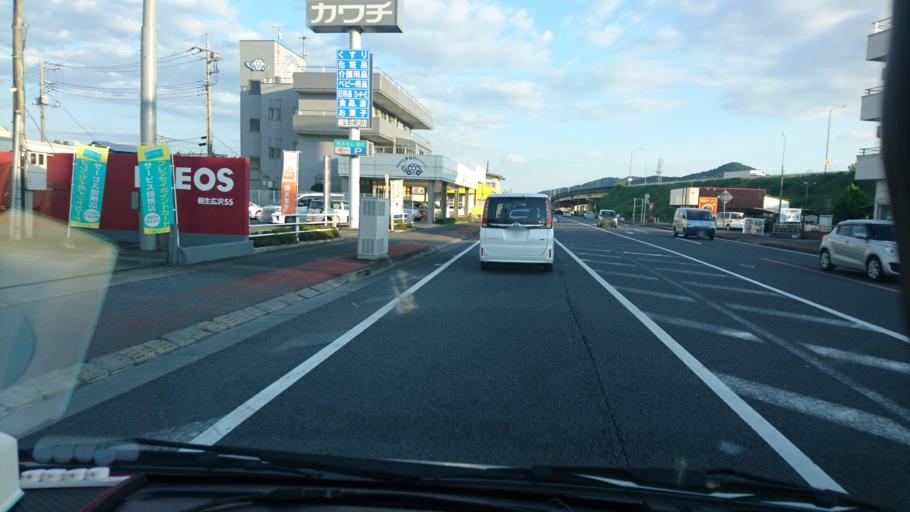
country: JP
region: Gunma
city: Kiryu
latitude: 36.3868
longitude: 139.3349
